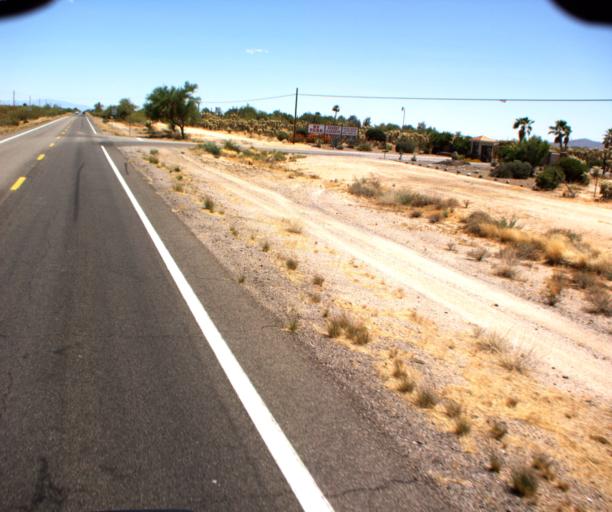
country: US
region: Arizona
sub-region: Pinal County
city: Florence
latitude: 32.9644
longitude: -111.3392
